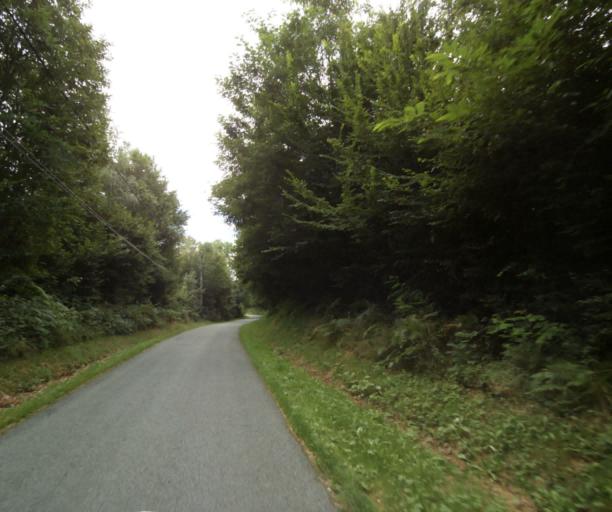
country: FR
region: Limousin
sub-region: Departement de la Correze
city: Sainte-Fortunade
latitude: 45.1978
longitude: 1.8093
